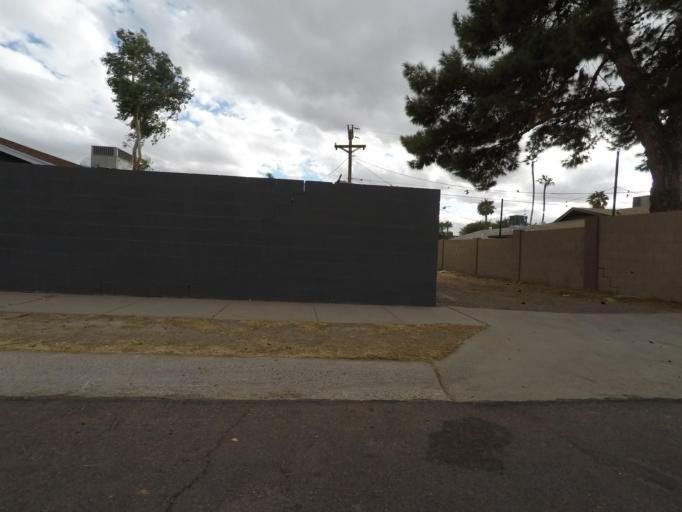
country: US
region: Arizona
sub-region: Maricopa County
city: Glendale
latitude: 33.5083
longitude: -112.1433
